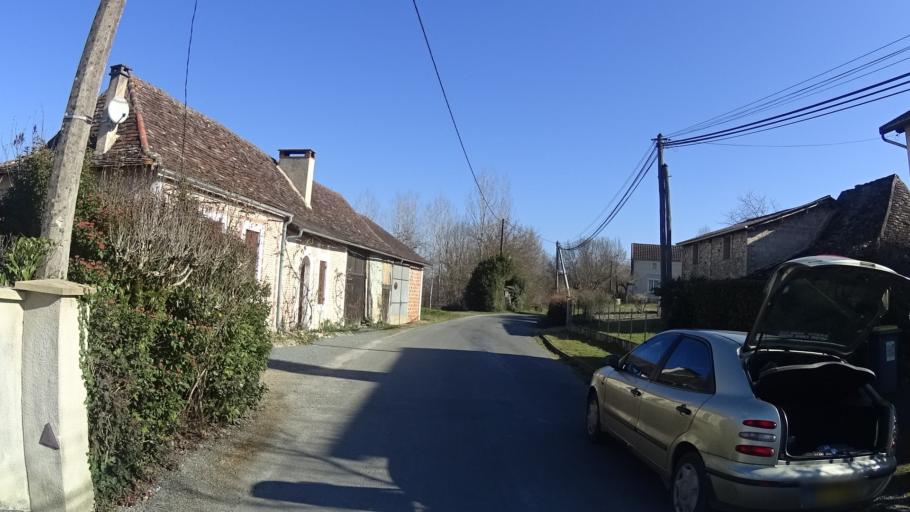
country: FR
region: Aquitaine
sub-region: Departement de la Dordogne
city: Montpon-Menesterol
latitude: 45.0386
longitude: 0.2543
